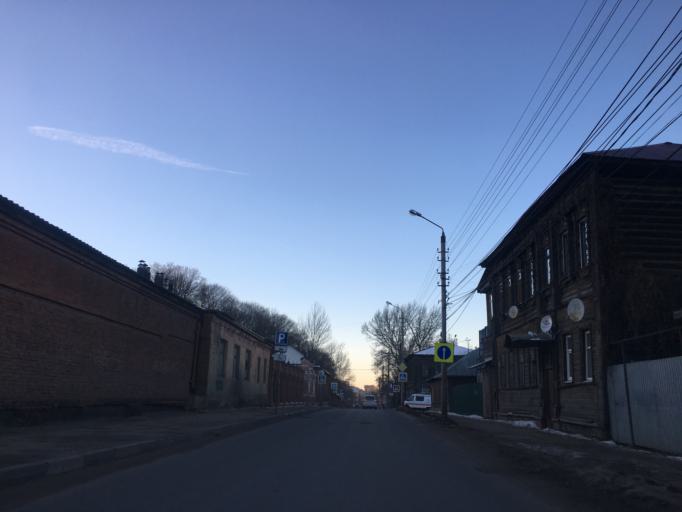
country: RU
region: Tula
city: Tula
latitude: 54.1812
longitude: 37.6139
